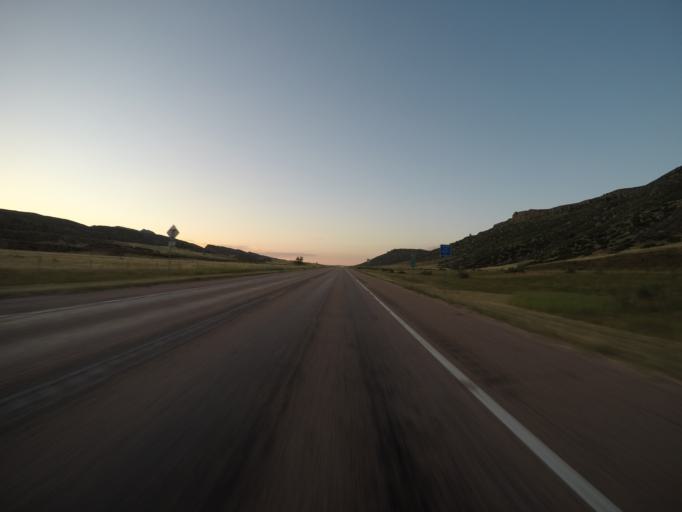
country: US
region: Colorado
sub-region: Larimer County
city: Laporte
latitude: 40.7010
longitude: -105.1740
